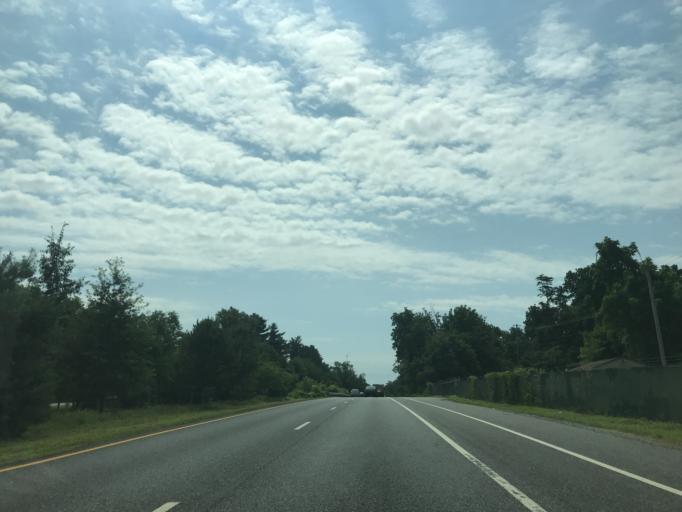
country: US
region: Maryland
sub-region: Montgomery County
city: Cabin John
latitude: 38.9790
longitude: -77.1315
